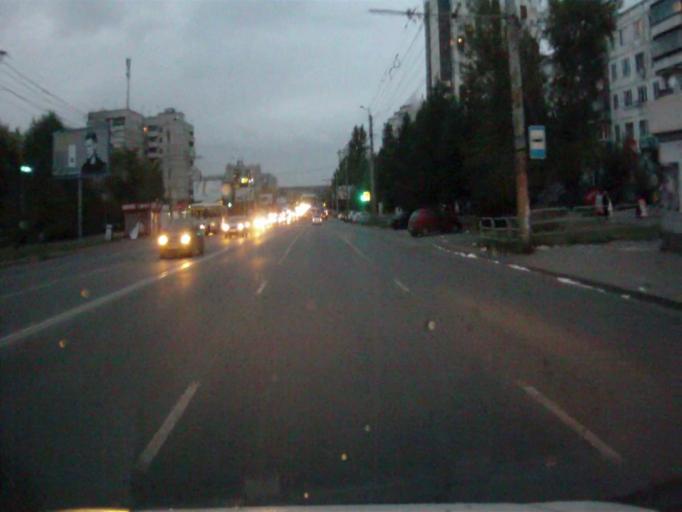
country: RU
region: Chelyabinsk
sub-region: Gorod Chelyabinsk
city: Chelyabinsk
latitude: 55.1837
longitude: 61.3326
